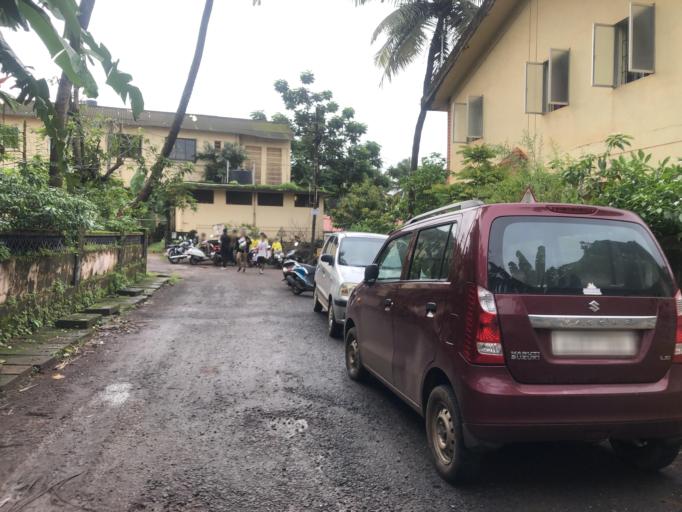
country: IN
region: Goa
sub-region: North Goa
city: Mapuca
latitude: 15.5951
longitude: 73.8045
